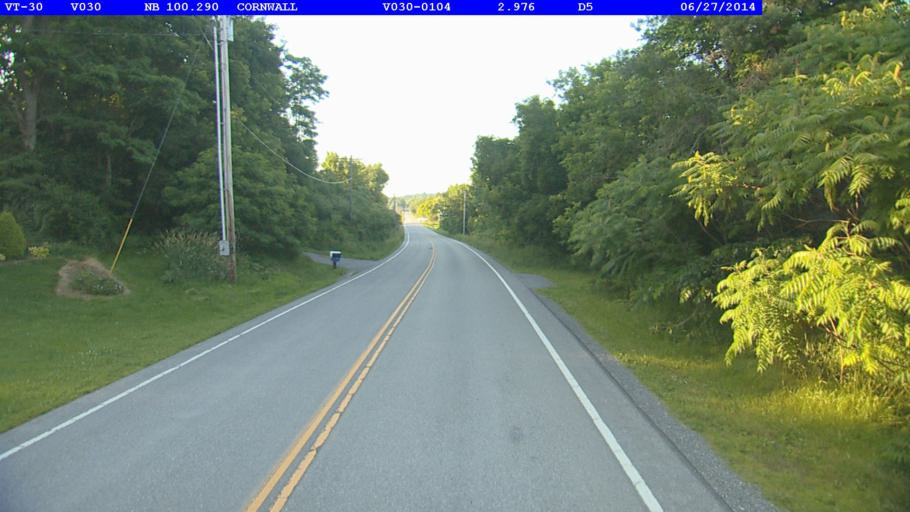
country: US
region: Vermont
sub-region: Addison County
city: Middlebury (village)
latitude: 43.9506
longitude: -73.2103
